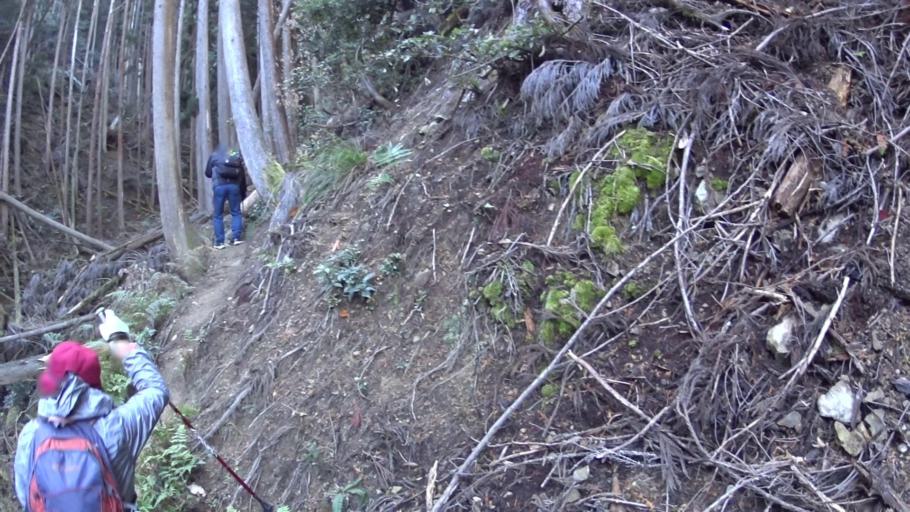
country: JP
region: Kyoto
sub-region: Kyoto-shi
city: Kamigyo-ku
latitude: 35.0874
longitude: 135.7333
